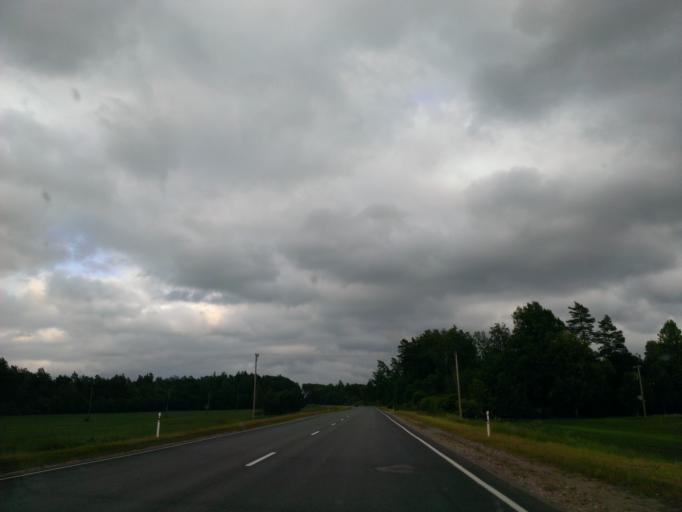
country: LV
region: Skrunda
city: Skrunda
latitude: 56.6775
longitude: 22.1467
